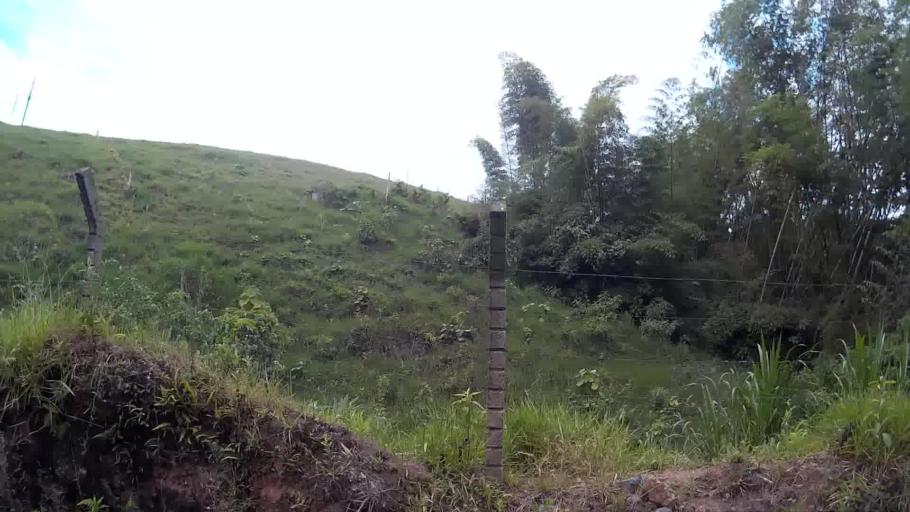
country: CO
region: Valle del Cauca
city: Ulloa
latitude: 4.7235
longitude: -75.7007
